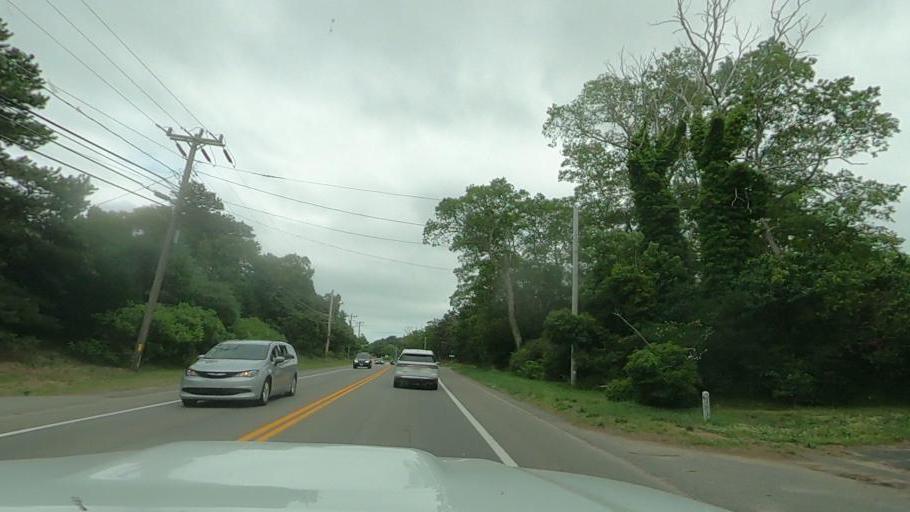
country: US
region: Massachusetts
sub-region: Barnstable County
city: Wellfleet
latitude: 41.9319
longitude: -70.0188
